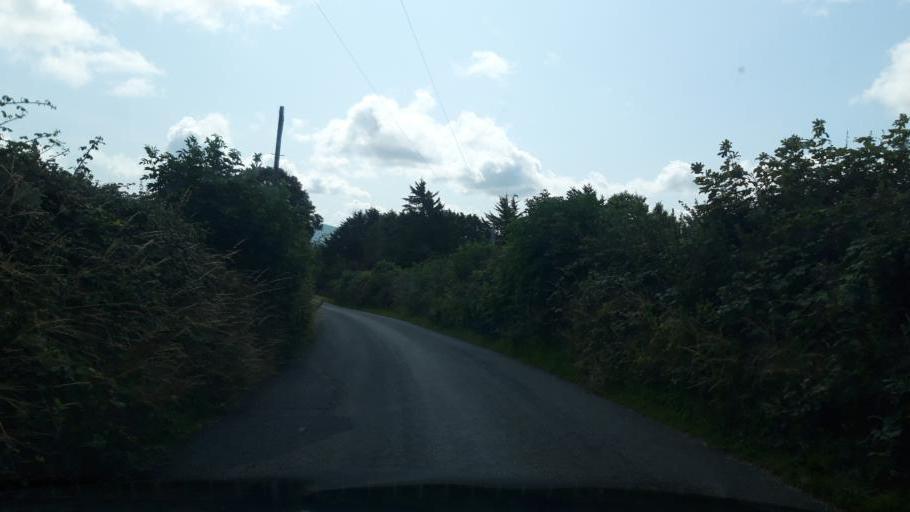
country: IE
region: Leinster
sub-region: Kilkenny
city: Graiguenamanagh
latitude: 52.5478
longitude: -6.9685
